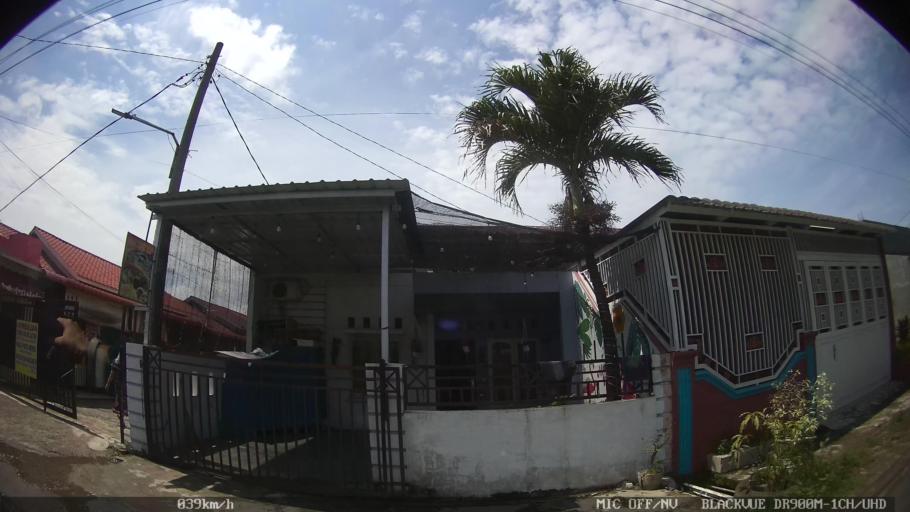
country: ID
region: North Sumatra
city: Medan
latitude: 3.6021
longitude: 98.7522
